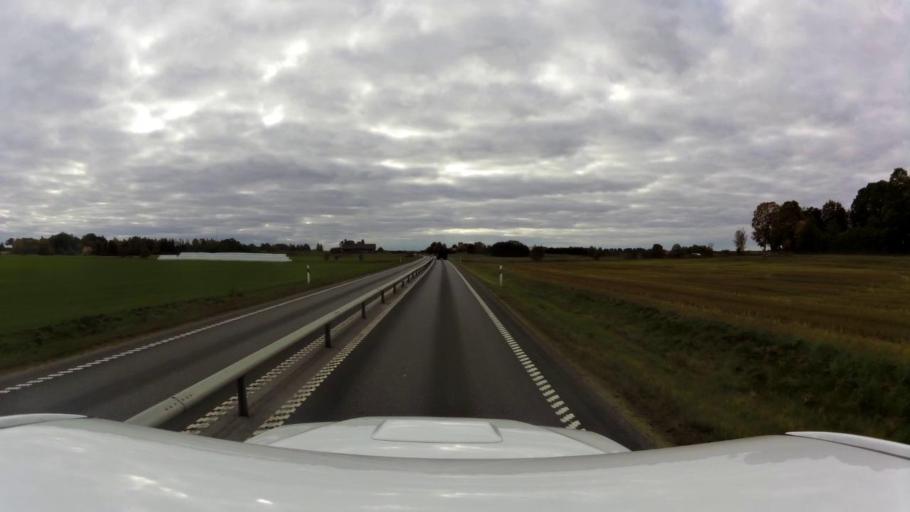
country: SE
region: OEstergoetland
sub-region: Linkopings Kommun
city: Malmslatt
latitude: 58.3405
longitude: 15.5546
